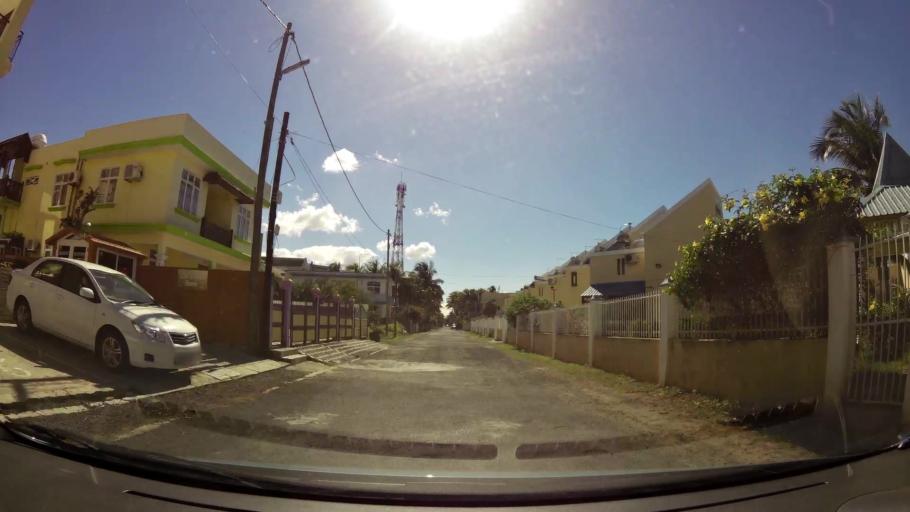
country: MU
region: Black River
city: Flic en Flac
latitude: -20.2928
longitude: 57.3650
